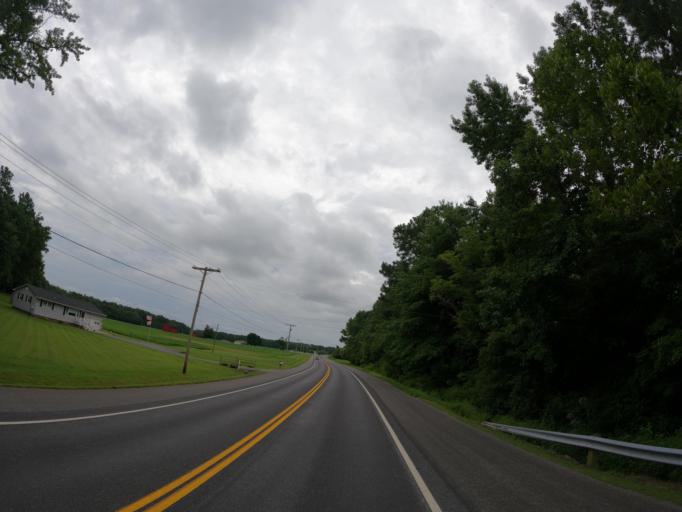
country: US
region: Maryland
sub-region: Saint Mary's County
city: Lexington Park
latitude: 38.1859
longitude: -76.5138
